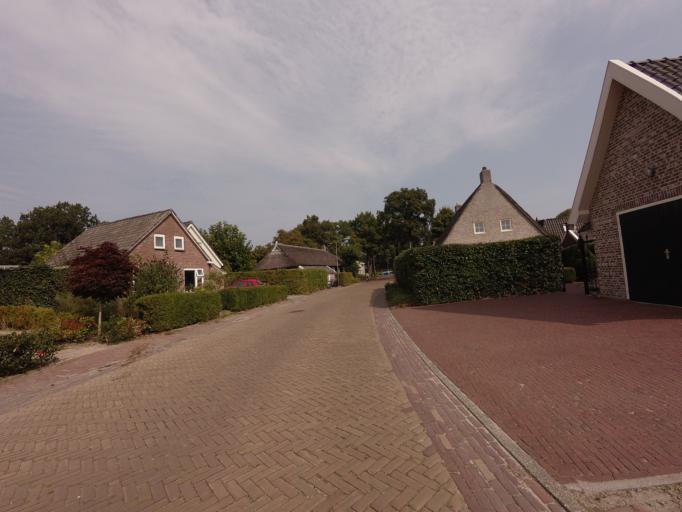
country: NL
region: Drenthe
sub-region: Gemeente Aa en Hunze
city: Anloo
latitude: 52.9863
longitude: 6.6444
